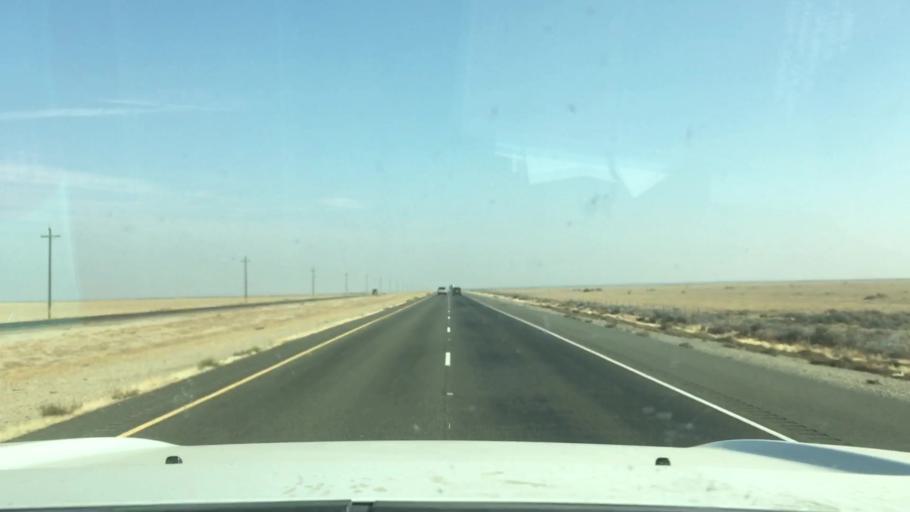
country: US
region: California
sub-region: Kern County
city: Lost Hills
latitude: 35.6156
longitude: -119.7959
